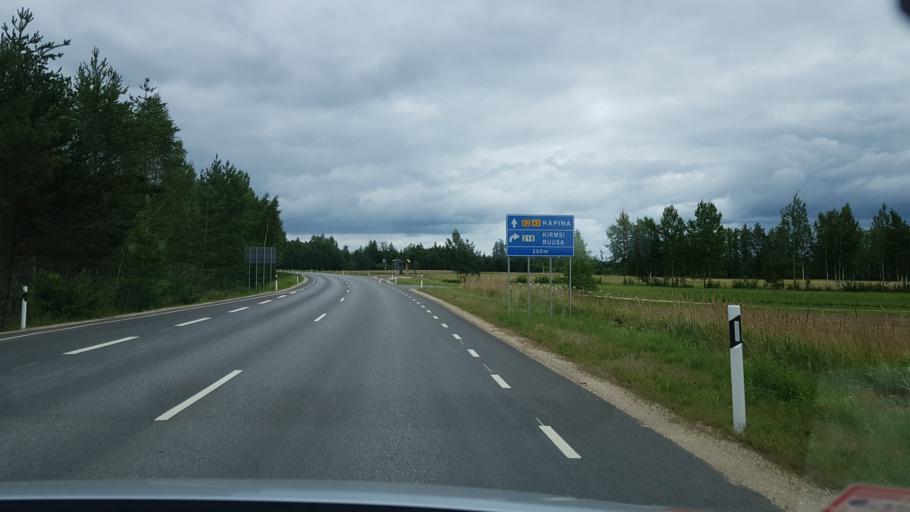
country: EE
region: Polvamaa
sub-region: Raepina vald
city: Rapina
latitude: 58.0710
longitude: 27.2742
